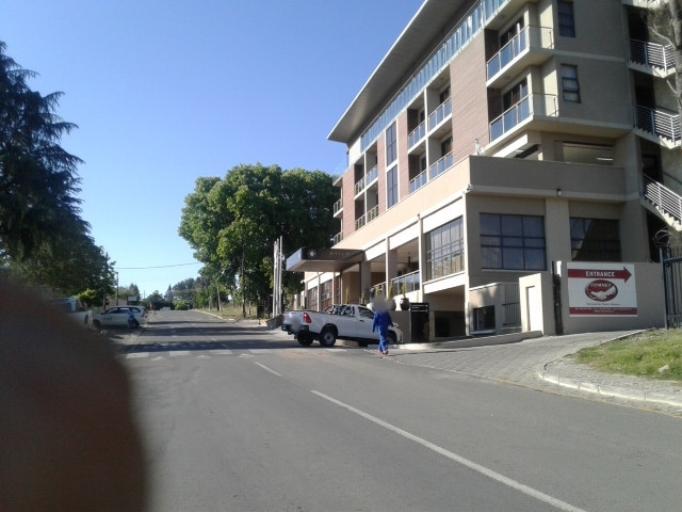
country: LS
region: Maseru
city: Maseru
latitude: -29.3078
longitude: 27.4727
